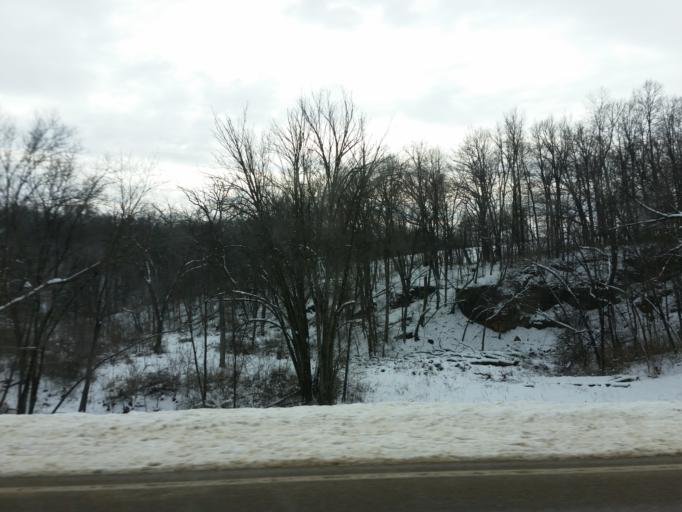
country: US
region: Iowa
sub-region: Dubuque County
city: Peosta
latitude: 42.3832
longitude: -90.7934
